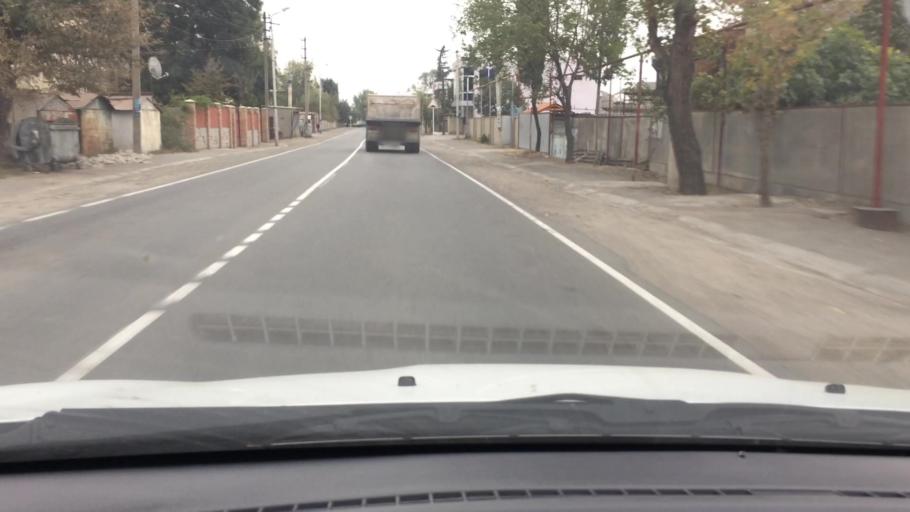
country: GE
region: Kvemo Kartli
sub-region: Marneuli
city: Marneuli
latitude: 41.4850
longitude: 44.8004
